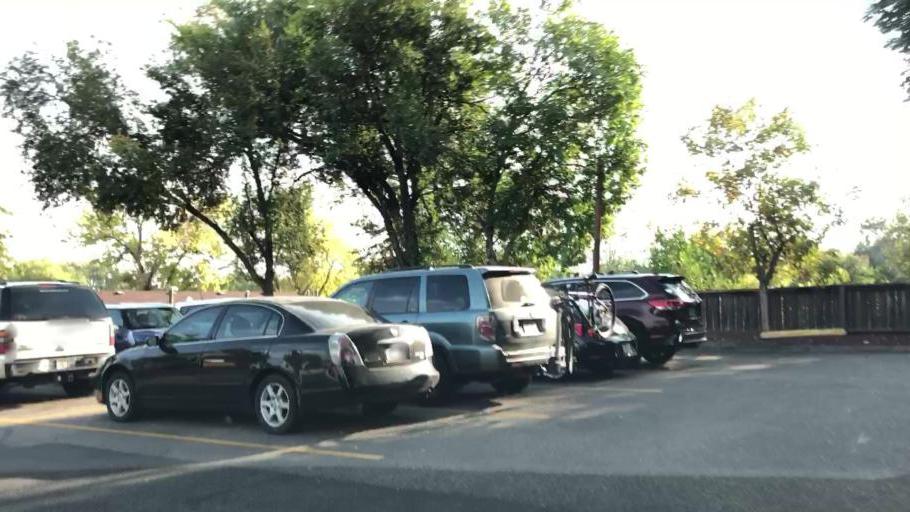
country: US
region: Colorado
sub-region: Larimer County
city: Fort Collins
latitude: 40.5642
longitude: -105.0763
